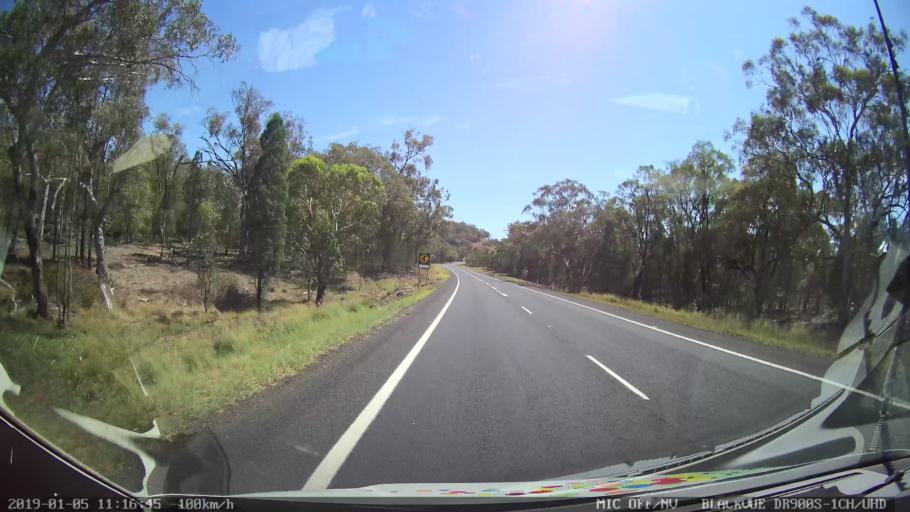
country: AU
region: New South Wales
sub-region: Warrumbungle Shire
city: Coonabarabran
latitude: -31.3347
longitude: 149.3007
